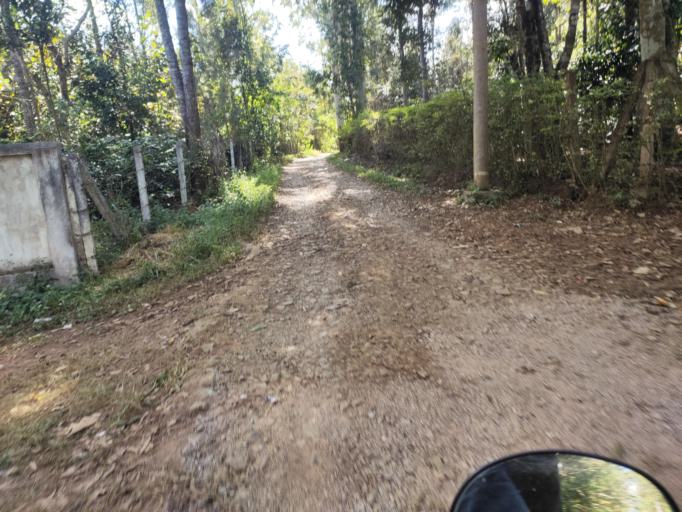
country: MM
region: Mandalay
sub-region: Pyin Oo Lwin District
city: Pyin Oo Lwin
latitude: 21.9860
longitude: 96.4665
